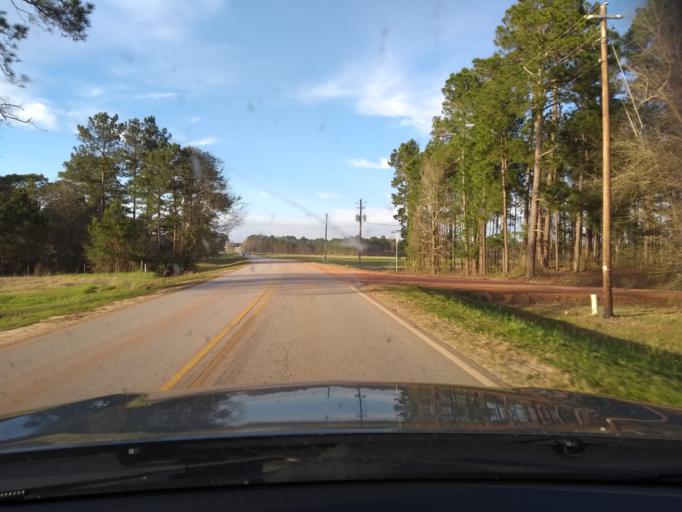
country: US
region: Georgia
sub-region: Bulloch County
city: Statesboro
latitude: 32.3482
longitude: -81.7713
